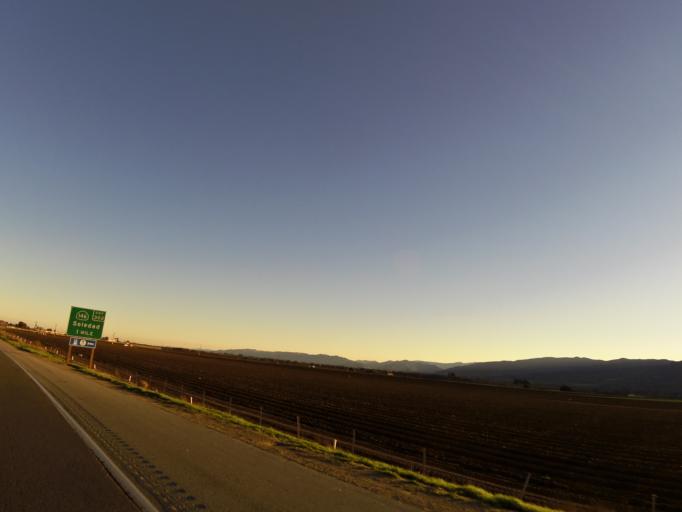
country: US
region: California
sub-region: Monterey County
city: Soledad
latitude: 36.4283
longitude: -121.3352
